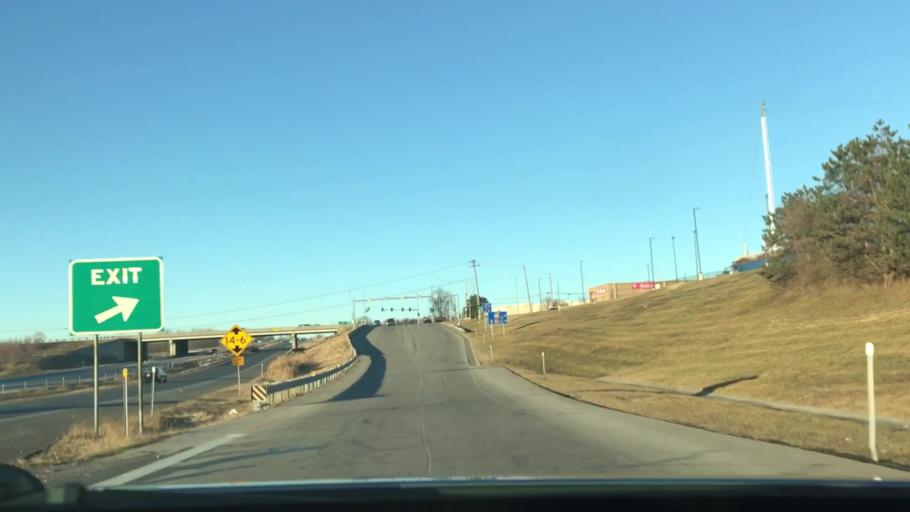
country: US
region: Missouri
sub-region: Clay County
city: Gladstone
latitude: 39.2440
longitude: -94.5901
